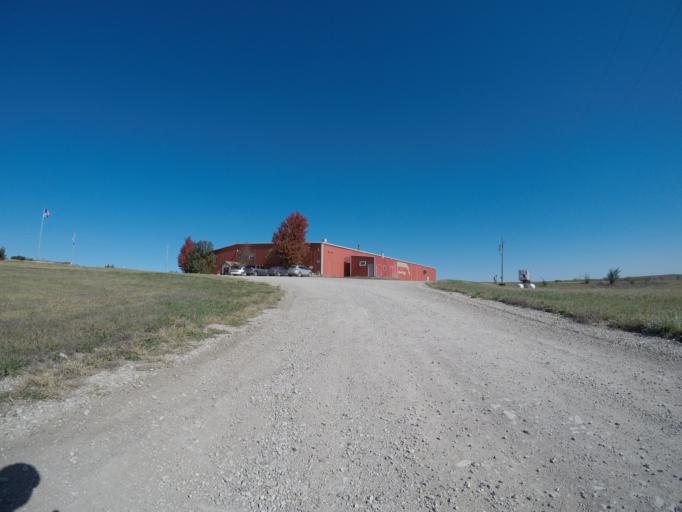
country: US
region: Kansas
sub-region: Wabaunsee County
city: Alma
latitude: 39.0681
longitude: -96.3491
